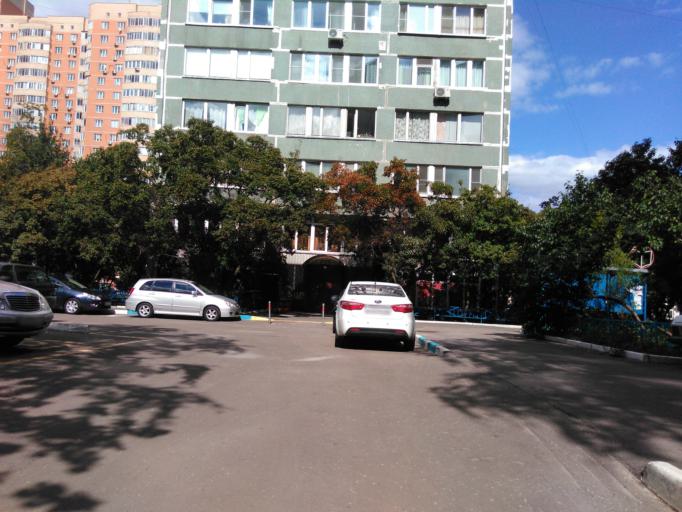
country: RU
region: Moskovskaya
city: Semenovskoye
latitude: 55.6673
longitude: 37.5228
